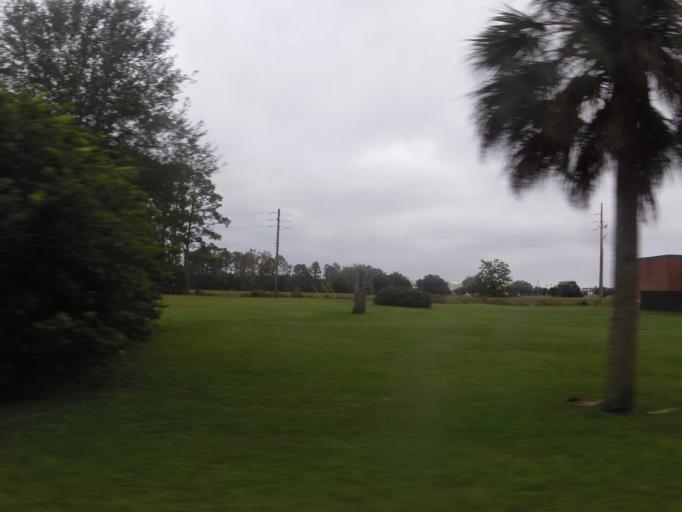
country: US
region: Florida
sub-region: Duval County
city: Baldwin
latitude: 30.2305
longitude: -81.8876
